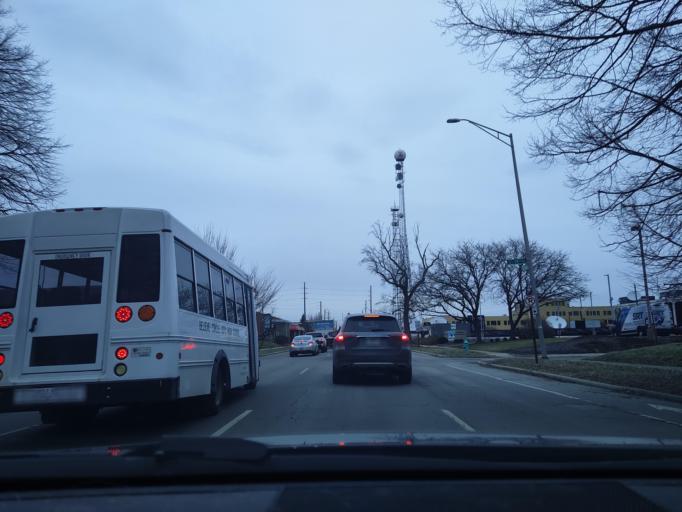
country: US
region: Indiana
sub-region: Marion County
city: Indianapolis
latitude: 39.7917
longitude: -86.1591
